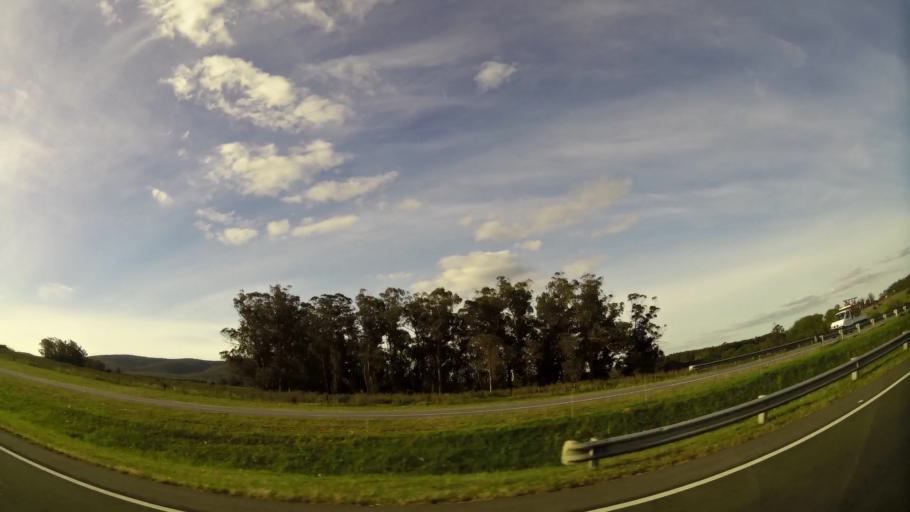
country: UY
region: Maldonado
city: Pan de Azucar
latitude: -34.7889
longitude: -55.2945
